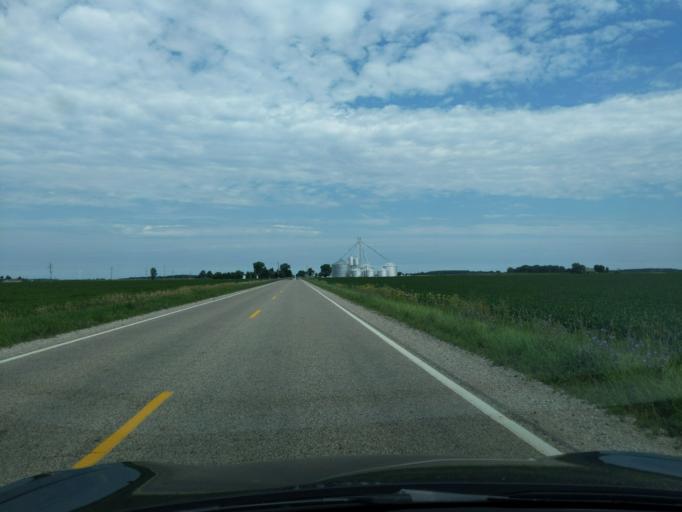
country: US
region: Michigan
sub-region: Gratiot County
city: Breckenridge
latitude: 43.3251
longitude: -84.4294
